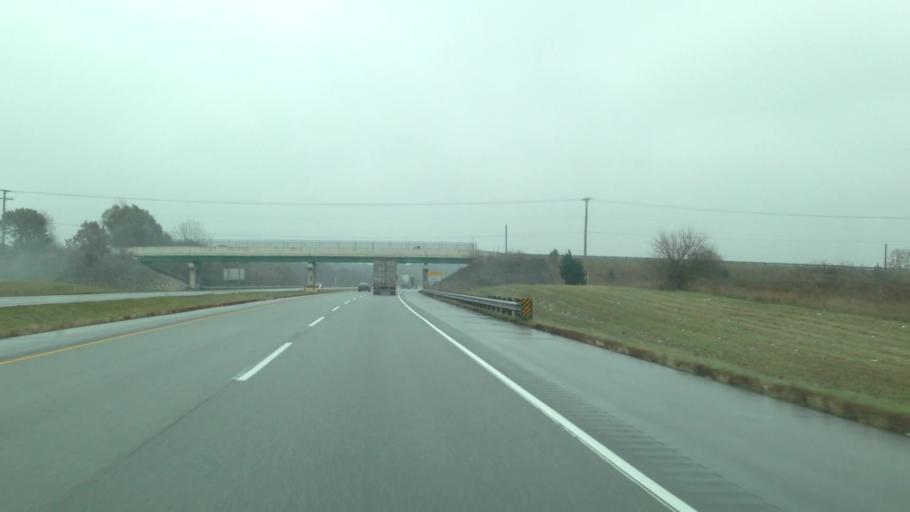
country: US
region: Indiana
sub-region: Saint Joseph County
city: Granger
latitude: 41.7338
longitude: -86.1127
